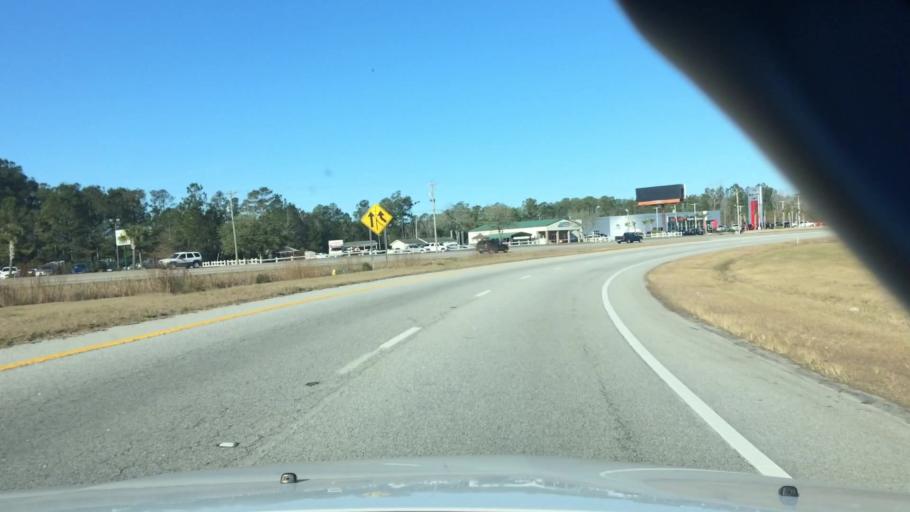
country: US
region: South Carolina
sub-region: Horry County
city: North Myrtle Beach
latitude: 33.8791
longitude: -78.6852
